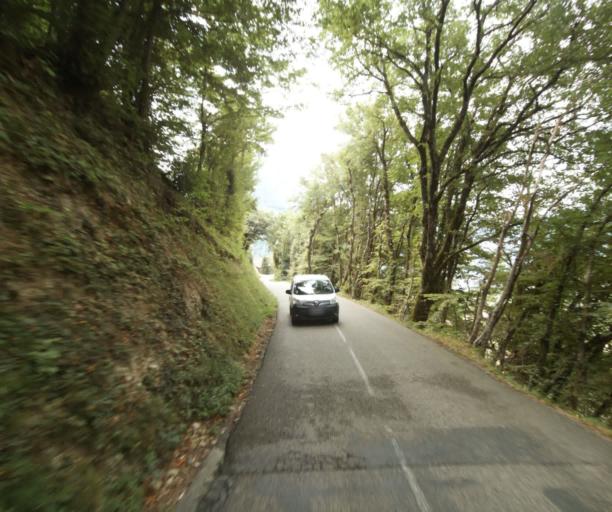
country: FR
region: Rhone-Alpes
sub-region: Departement de l'Isere
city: Saint-Egreve
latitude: 45.2610
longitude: 5.7079
